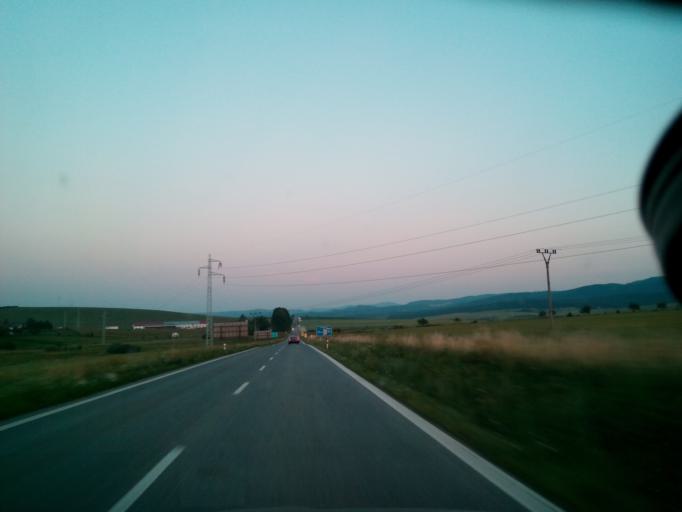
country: SK
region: Kosicky
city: Spisska Nova Ves
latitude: 48.9784
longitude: 20.4862
